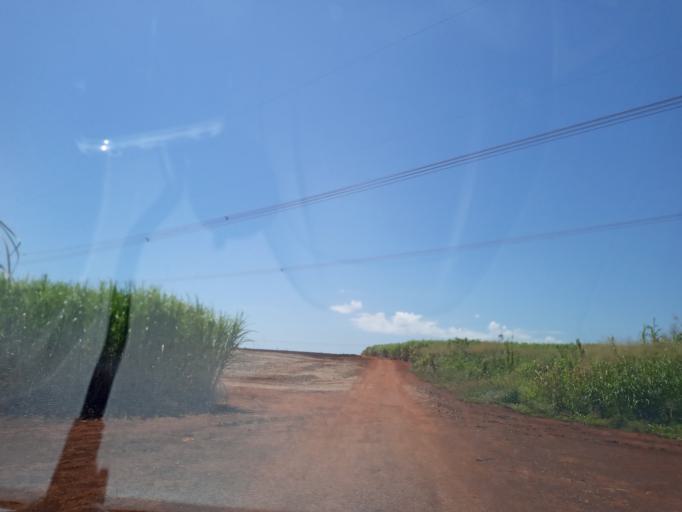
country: BR
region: Goias
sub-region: Itumbiara
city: Itumbiara
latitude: -18.4407
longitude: -49.1369
